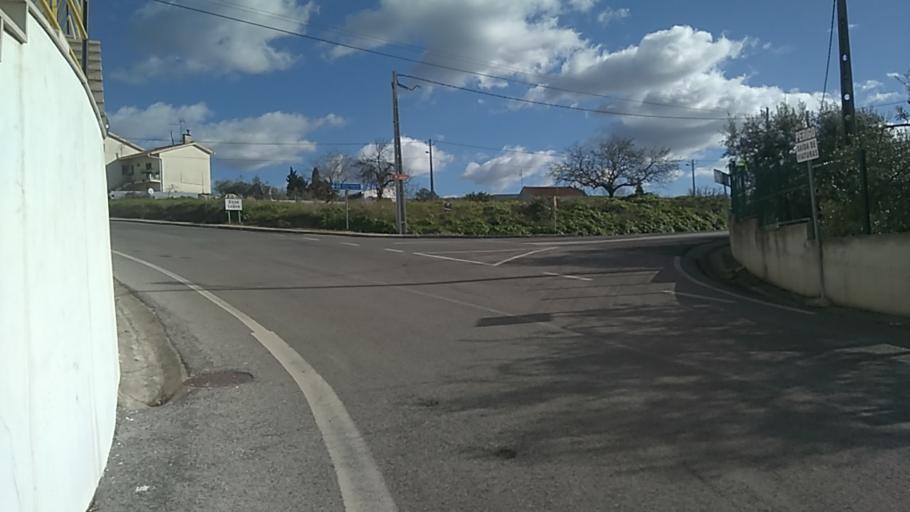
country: PT
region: Leiria
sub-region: Porto de Mos
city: Porto de Mos
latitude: 39.6028
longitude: -8.8124
